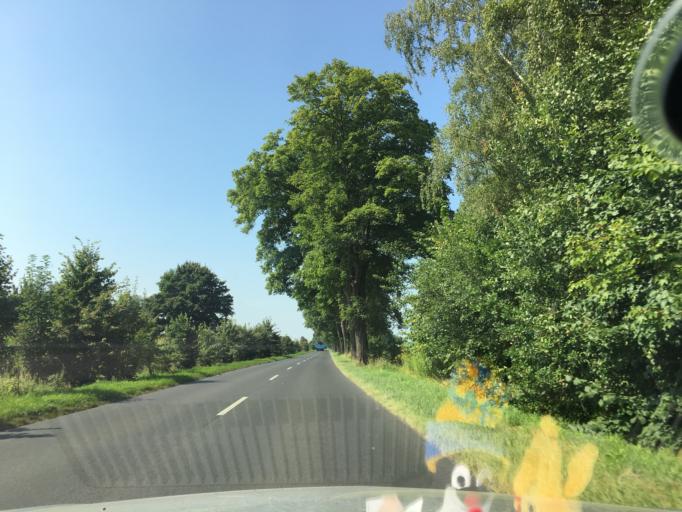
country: PL
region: West Pomeranian Voivodeship
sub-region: Powiat kamienski
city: Kamien Pomorski
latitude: 53.9980
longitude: 14.8286
